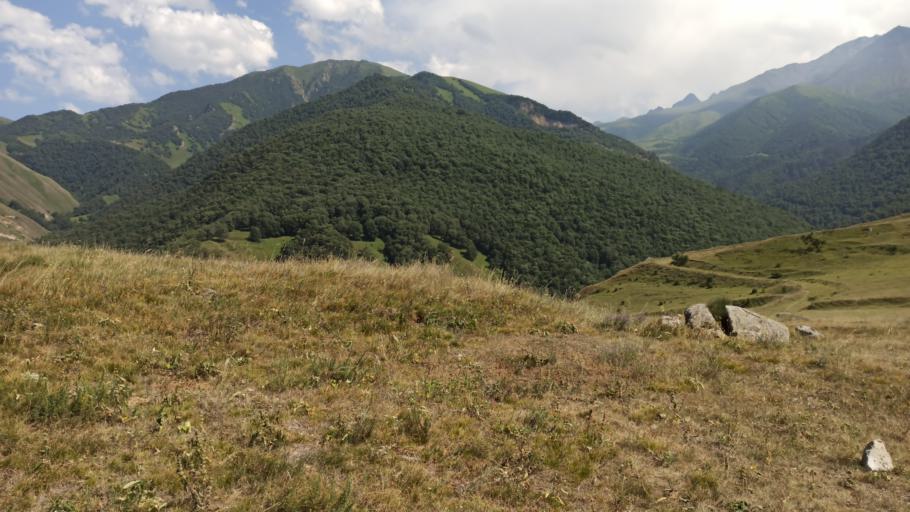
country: RU
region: Kabardino-Balkariya
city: Tyrnyauz
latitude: 43.3865
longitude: 42.9265
